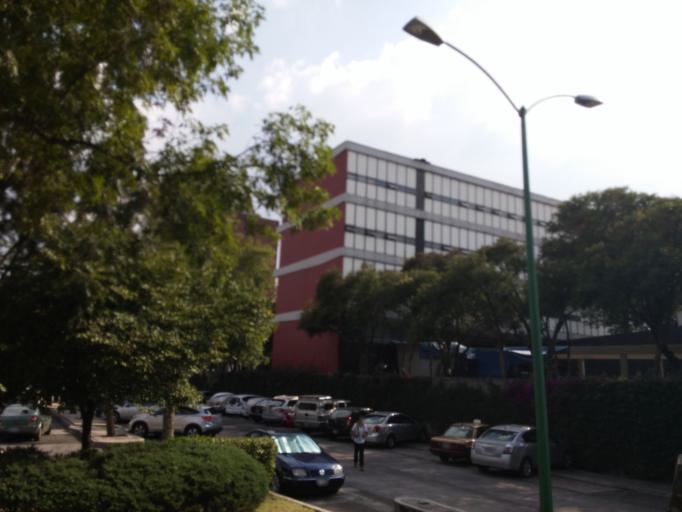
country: MX
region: Mexico City
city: Coyoacan
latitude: 19.3351
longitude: -99.1827
